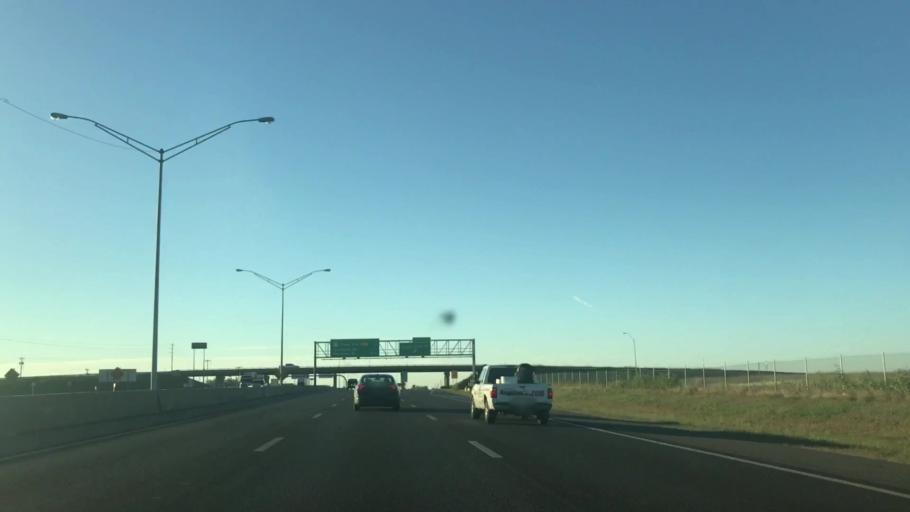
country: US
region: Oklahoma
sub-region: Cleveland County
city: Moore
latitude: 35.2931
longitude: -97.4885
